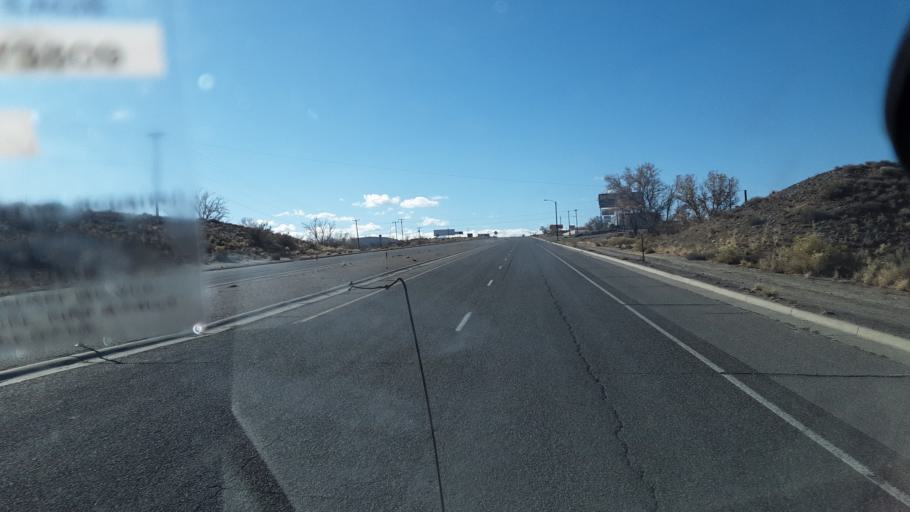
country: US
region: New Mexico
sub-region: San Juan County
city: Bloomfield
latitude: 36.6962
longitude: -107.9880
